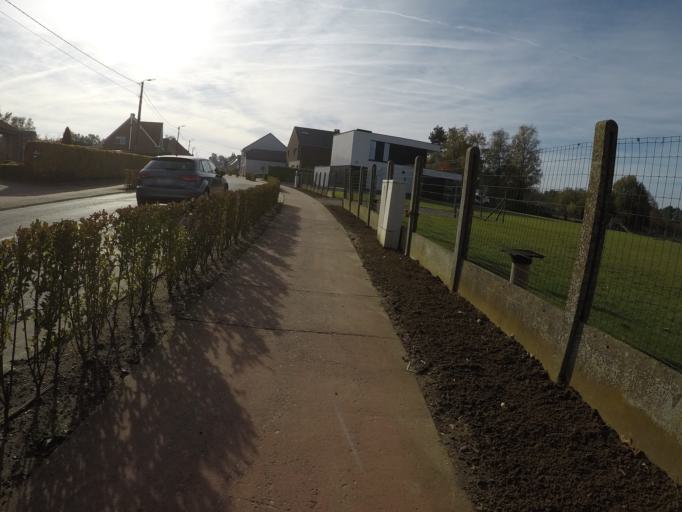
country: BE
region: Flanders
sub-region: Provincie Vlaams-Brabant
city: Begijnendijk
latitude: 51.0049
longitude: 4.7884
